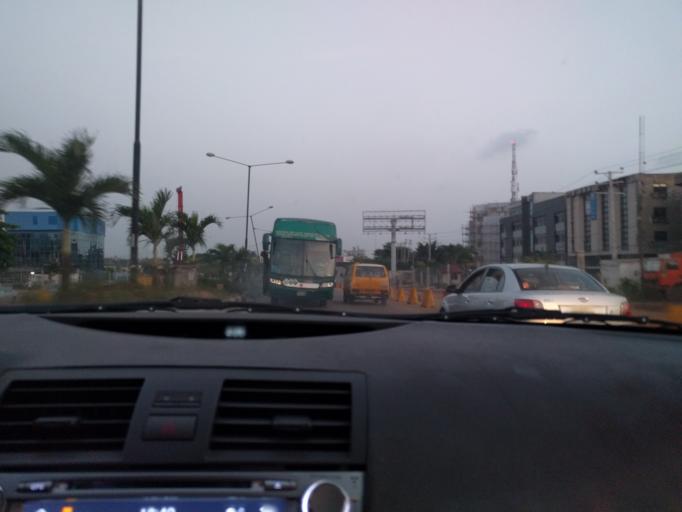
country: NG
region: Lagos
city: Oshodi
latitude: 6.5504
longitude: 3.3330
